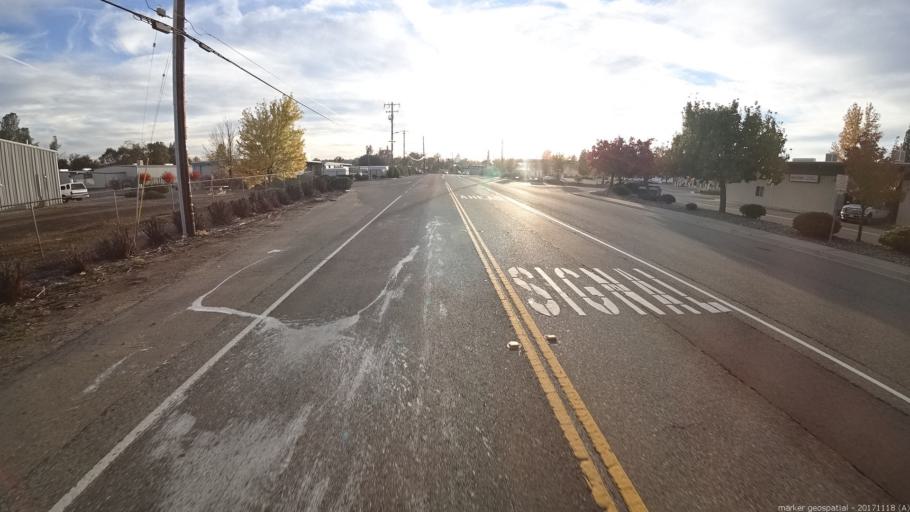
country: US
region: California
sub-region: Shasta County
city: Anderson
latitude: 40.4658
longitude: -122.3206
